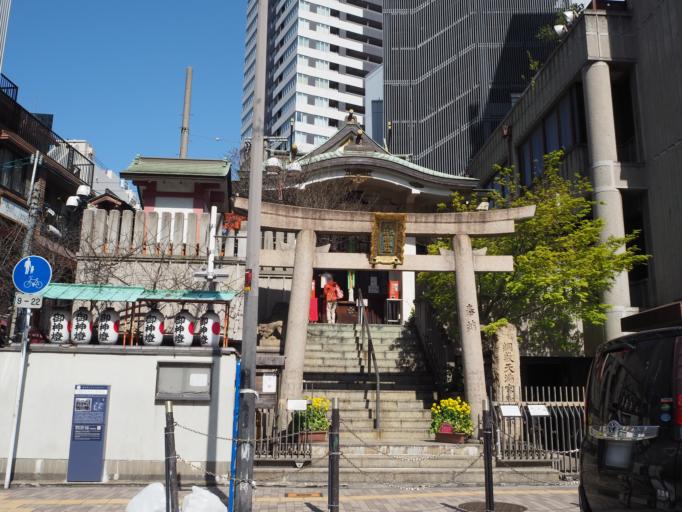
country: JP
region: Osaka
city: Osaka-shi
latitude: 34.7071
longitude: 135.4984
